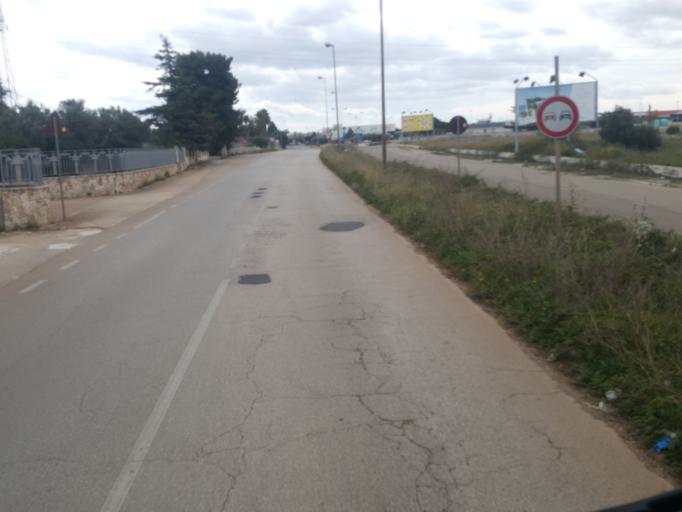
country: IT
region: Apulia
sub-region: Provincia di Bari
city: Conversano
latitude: 40.9828
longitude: 17.1197
